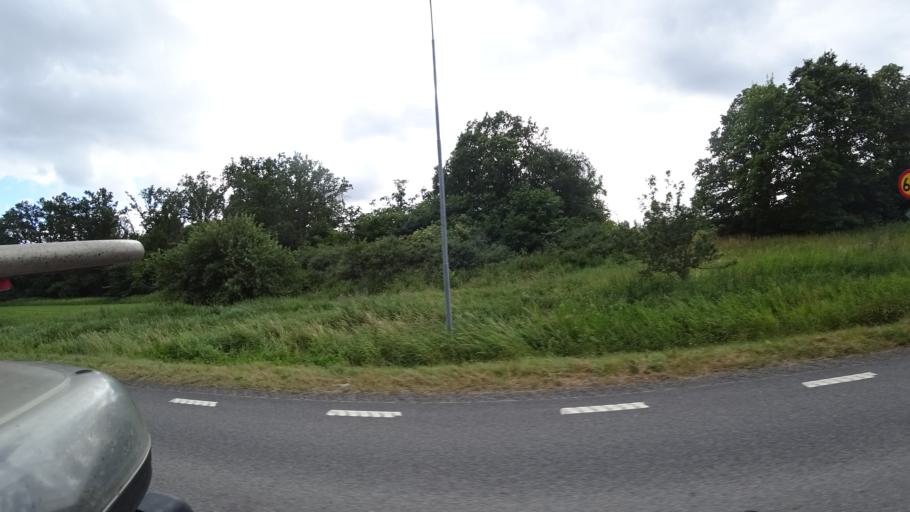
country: SE
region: Skane
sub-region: Ostra Goinge Kommun
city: Hanaskog
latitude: 56.1517
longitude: 14.0993
